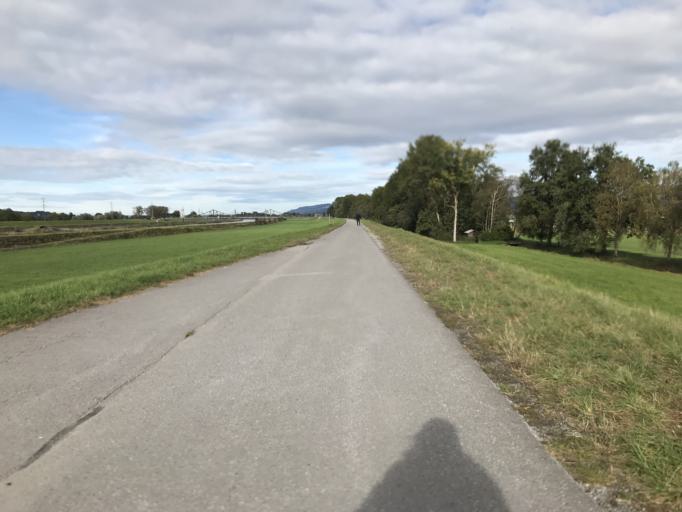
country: CH
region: Saint Gallen
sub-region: Wahlkreis Rheintal
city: Diepoldsau
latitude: 47.3753
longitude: 9.6372
